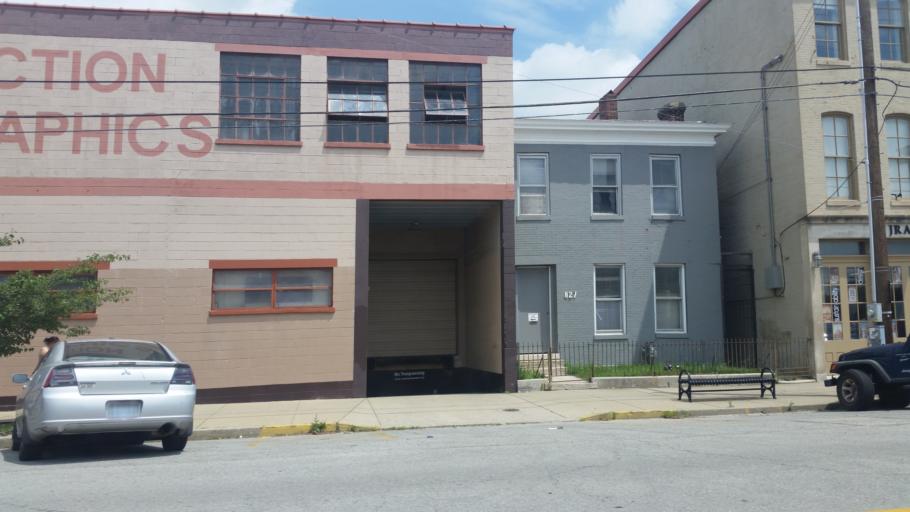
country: US
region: Kentucky
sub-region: Jefferson County
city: Louisville
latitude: 38.2532
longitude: -85.7368
